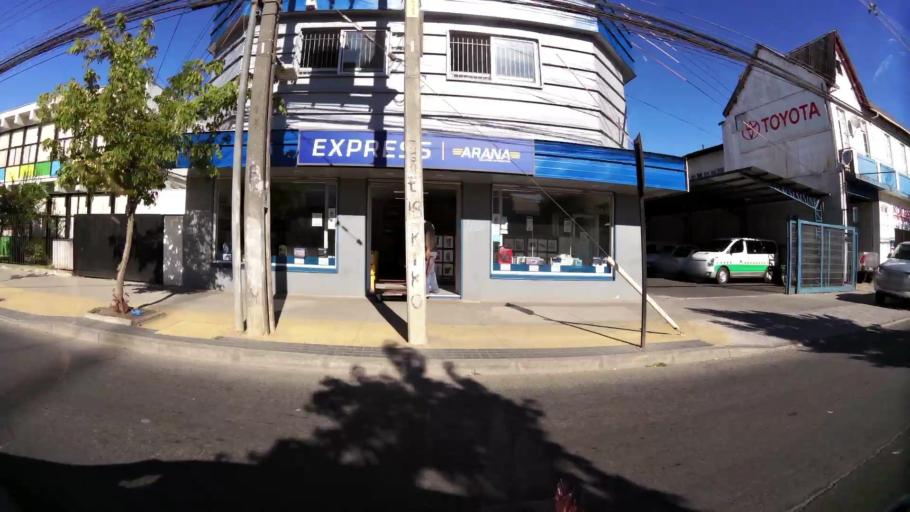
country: CL
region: O'Higgins
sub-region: Provincia de Colchagua
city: Chimbarongo
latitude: -34.5898
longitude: -70.9859
